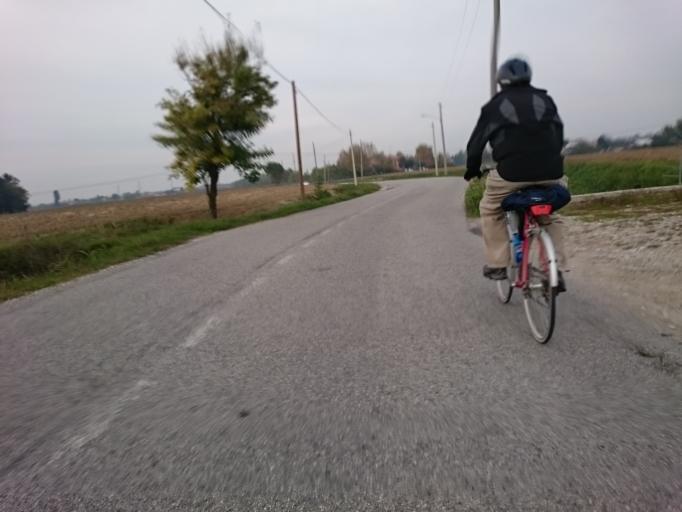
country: IT
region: Veneto
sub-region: Provincia di Padova
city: Albignasego
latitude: 45.3551
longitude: 11.8838
